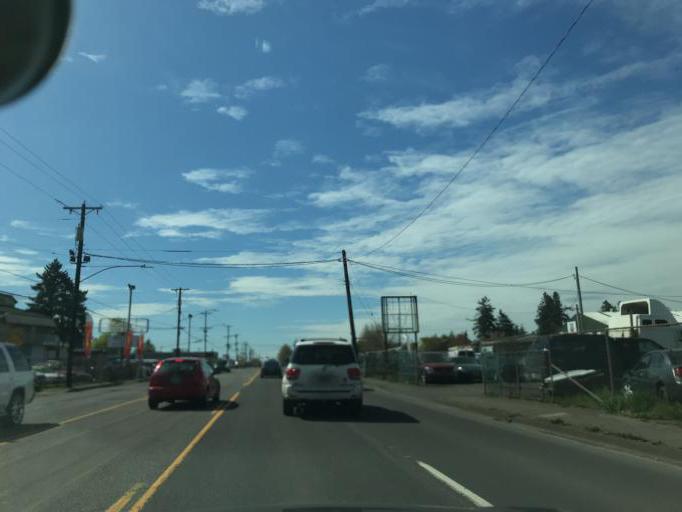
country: US
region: Oregon
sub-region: Multnomah County
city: Lents
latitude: 45.4626
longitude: -122.5791
